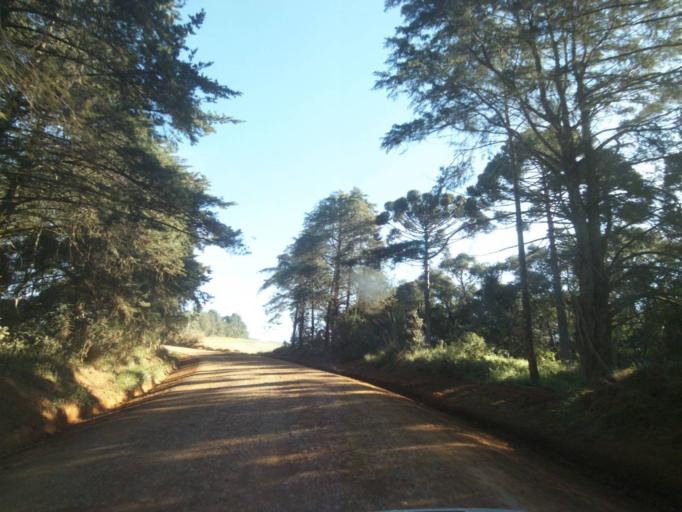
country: BR
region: Parana
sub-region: Tibagi
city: Tibagi
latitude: -24.5263
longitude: -50.5095
